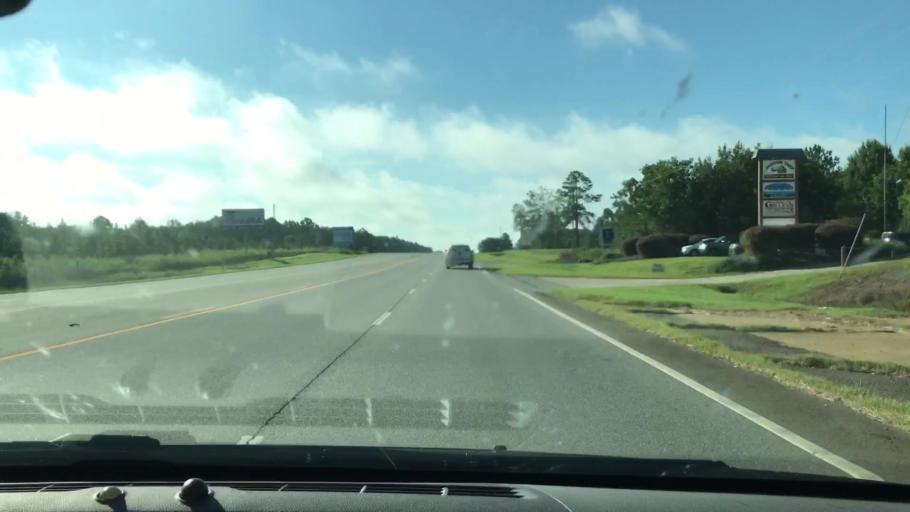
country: US
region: Georgia
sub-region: Terrell County
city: Dawson
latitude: 31.7546
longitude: -84.4254
